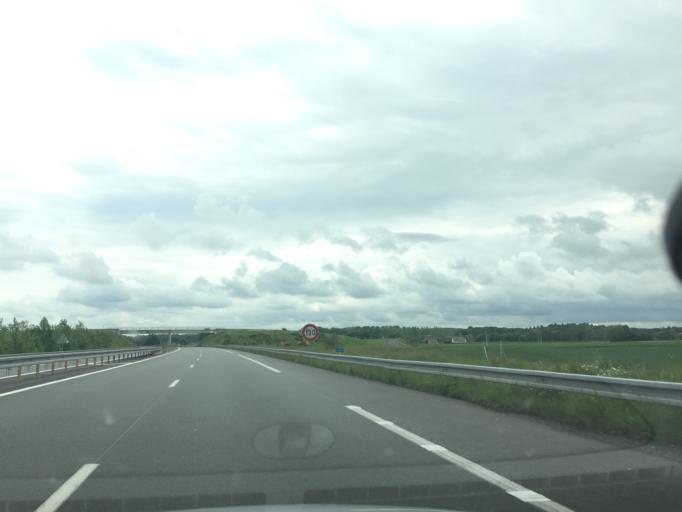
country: FR
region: Pays de la Loire
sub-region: Departement de la Sarthe
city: Luceau
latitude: 47.6727
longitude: 0.3726
